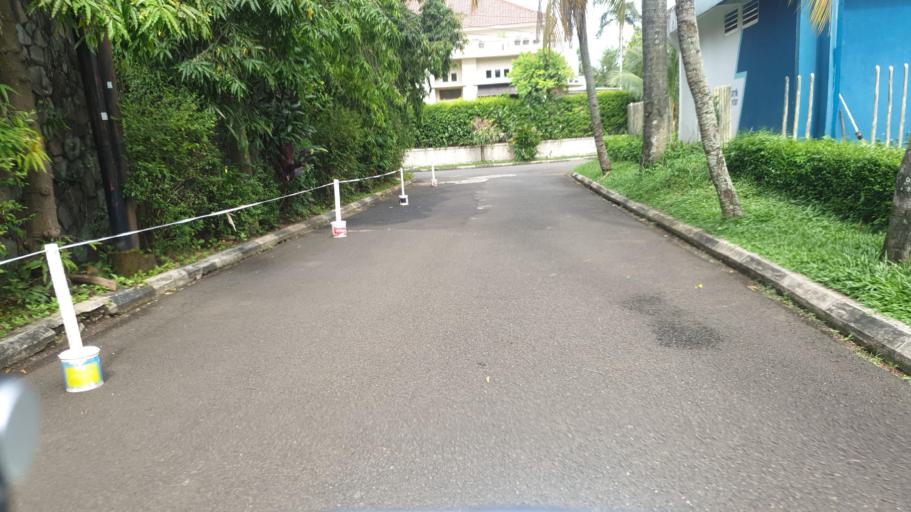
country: ID
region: West Java
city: Pamulang
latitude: -6.2943
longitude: 106.7913
